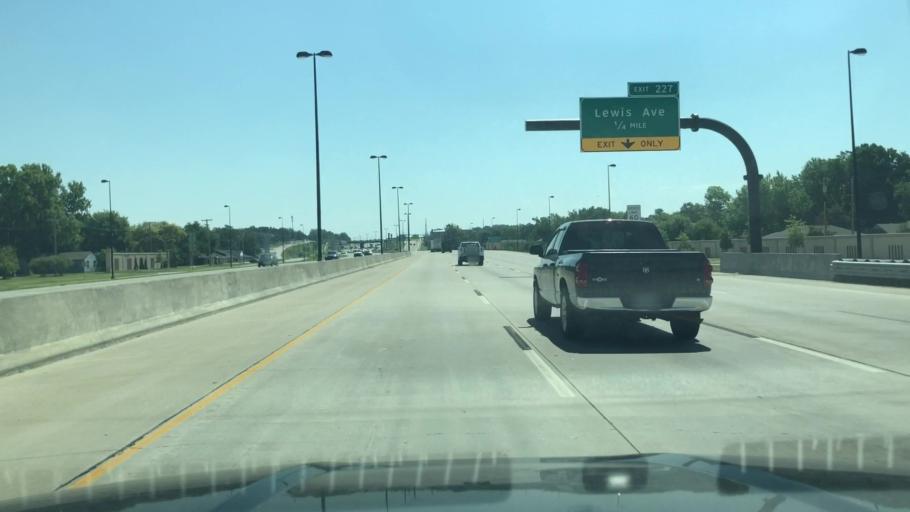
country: US
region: Oklahoma
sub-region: Tulsa County
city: Jenks
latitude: 36.0895
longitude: -95.9694
